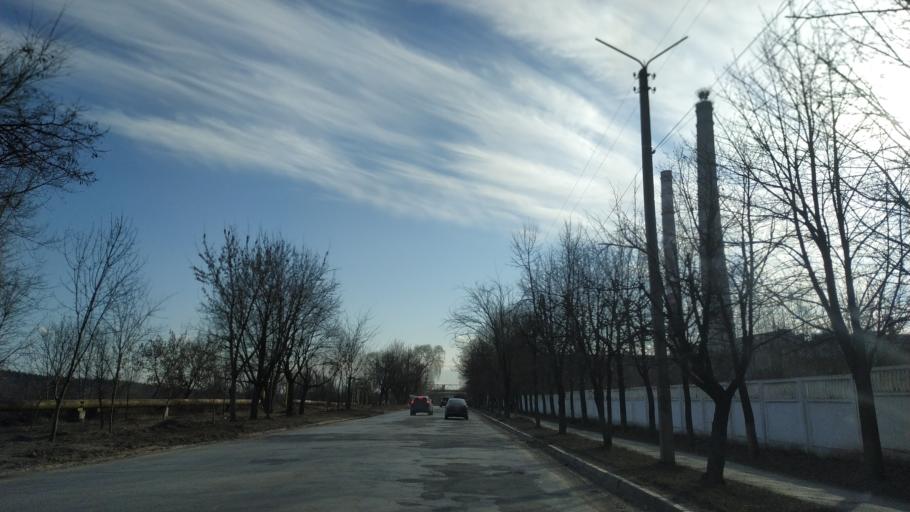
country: MD
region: Chisinau
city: Chisinau
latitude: 47.0336
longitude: 28.8972
